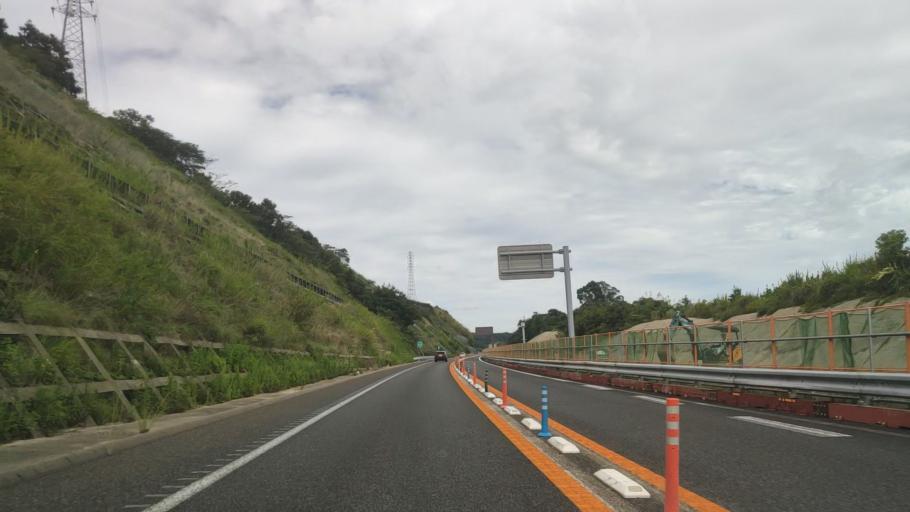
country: JP
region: Wakayama
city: Gobo
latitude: 33.8292
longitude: 135.2194
